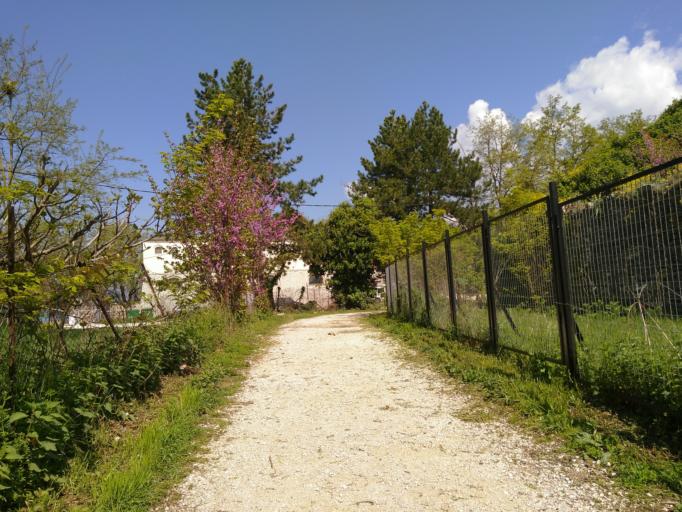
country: GR
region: Epirus
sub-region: Nomos Ioanninon
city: Ioannina
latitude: 39.6723
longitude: 20.8596
